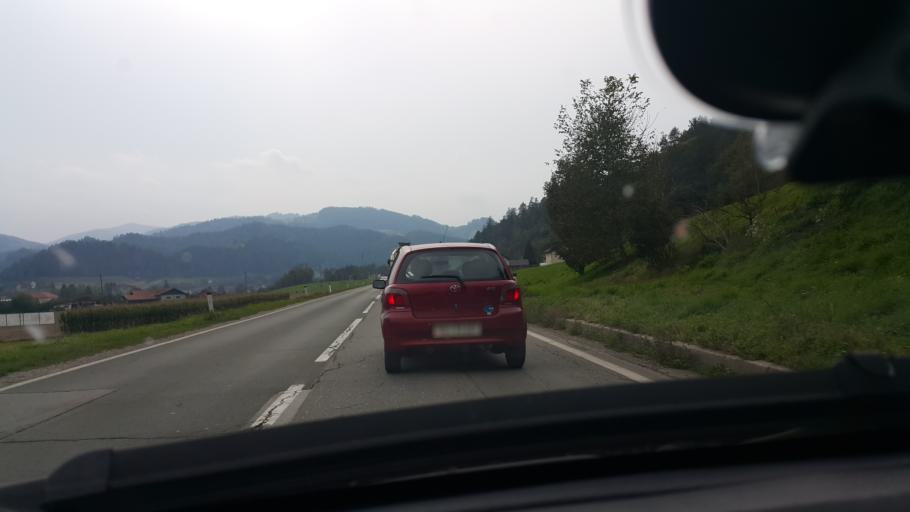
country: SI
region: Muta
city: Muta
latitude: 46.6072
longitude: 15.1673
